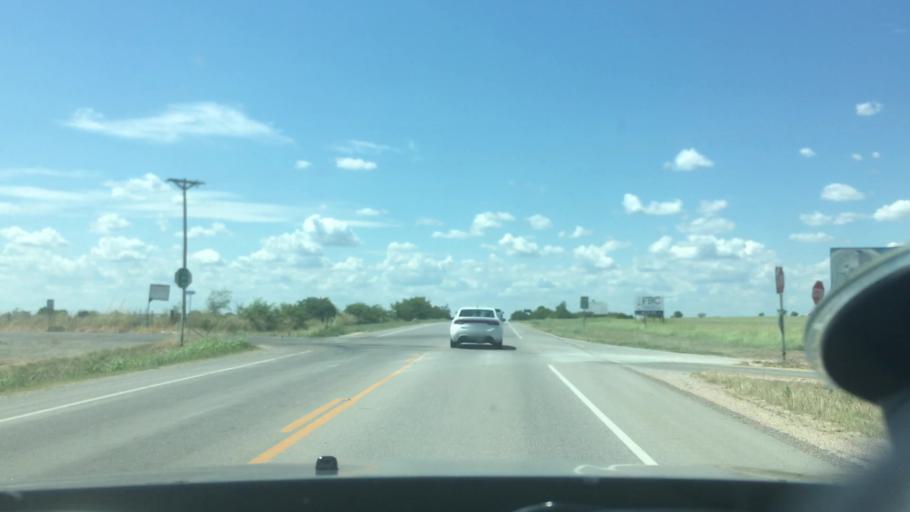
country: US
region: Oklahoma
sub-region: Marshall County
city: Madill
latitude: 34.0510
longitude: -96.7437
